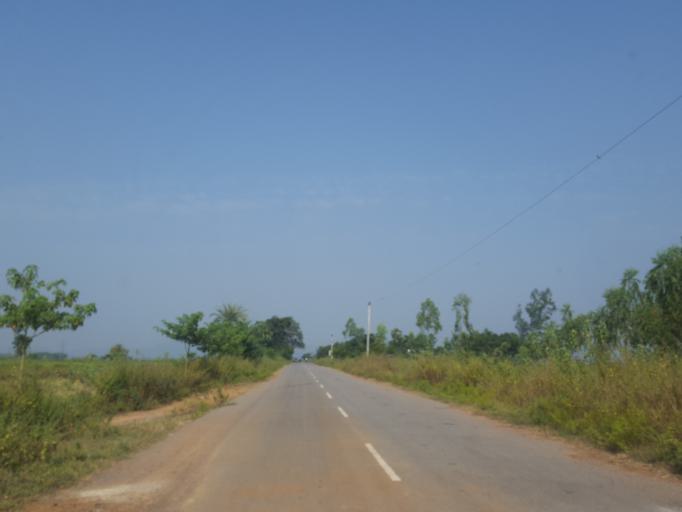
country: IN
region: Telangana
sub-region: Khammam
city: Yellandu
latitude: 17.6468
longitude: 80.2923
